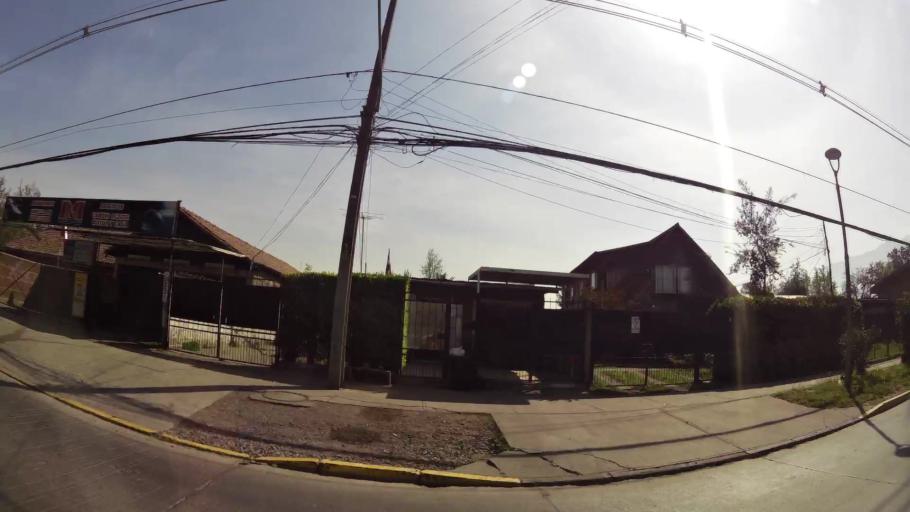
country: CL
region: Santiago Metropolitan
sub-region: Provincia de Santiago
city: Villa Presidente Frei, Nunoa, Santiago, Chile
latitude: -33.5224
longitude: -70.5757
